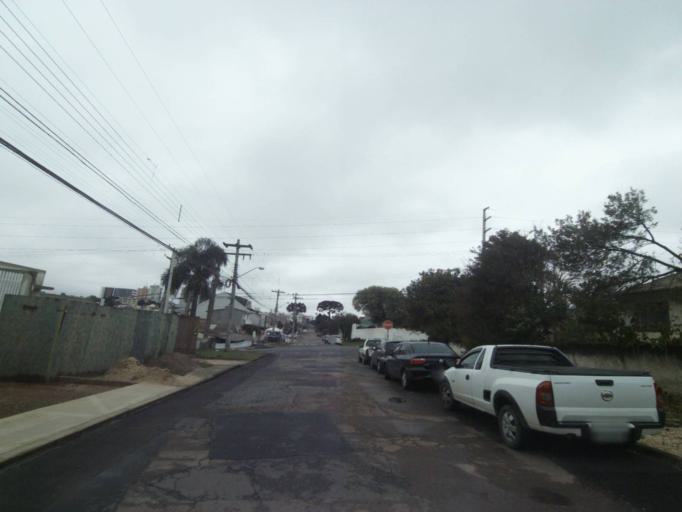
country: BR
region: Parana
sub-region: Curitiba
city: Curitiba
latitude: -25.5162
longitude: -49.3048
